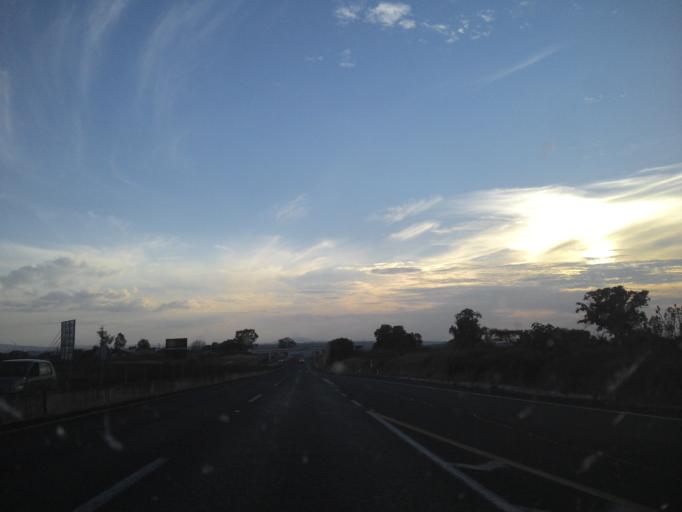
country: MX
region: Jalisco
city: Tepatitlan de Morelos
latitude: 20.8197
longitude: -102.7986
